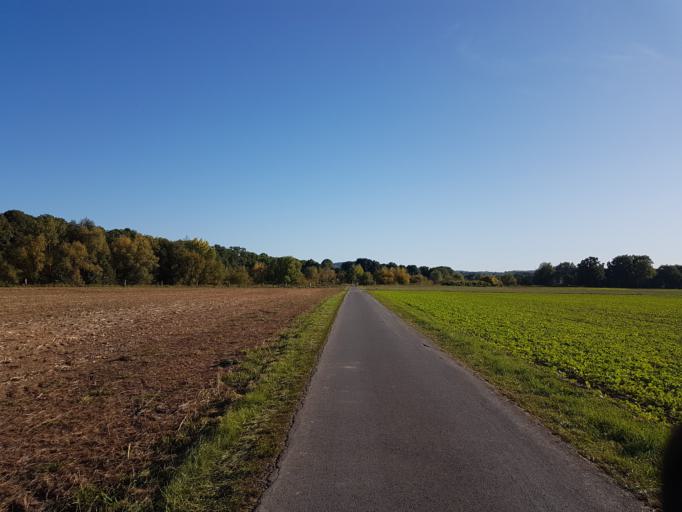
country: DE
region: North Rhine-Westphalia
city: Bad Oeynhausen
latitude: 52.2289
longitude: 8.8362
